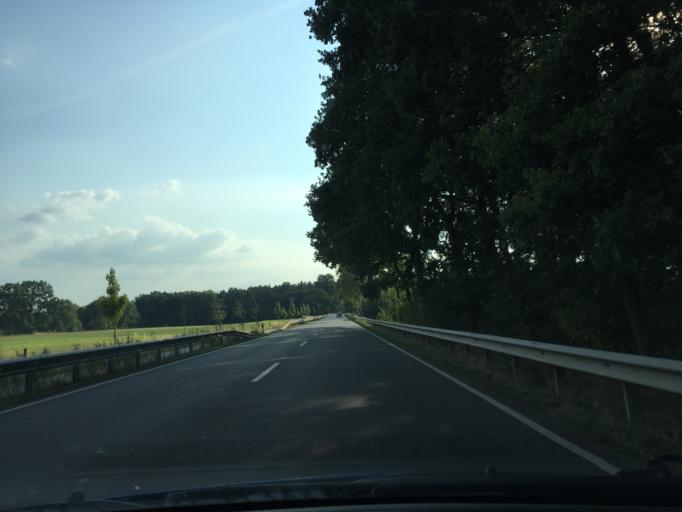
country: DE
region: Lower Saxony
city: Zernien
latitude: 53.0613
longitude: 10.8483
